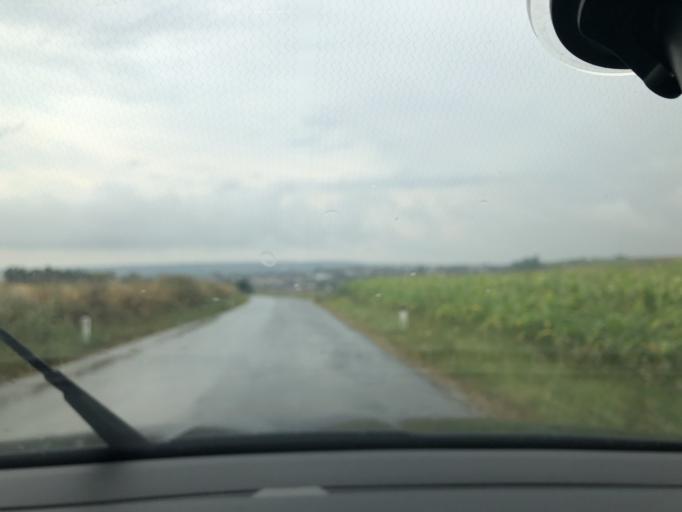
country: AT
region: Lower Austria
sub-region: Politischer Bezirk Ganserndorf
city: Auersthal
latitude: 48.3853
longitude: 16.6512
